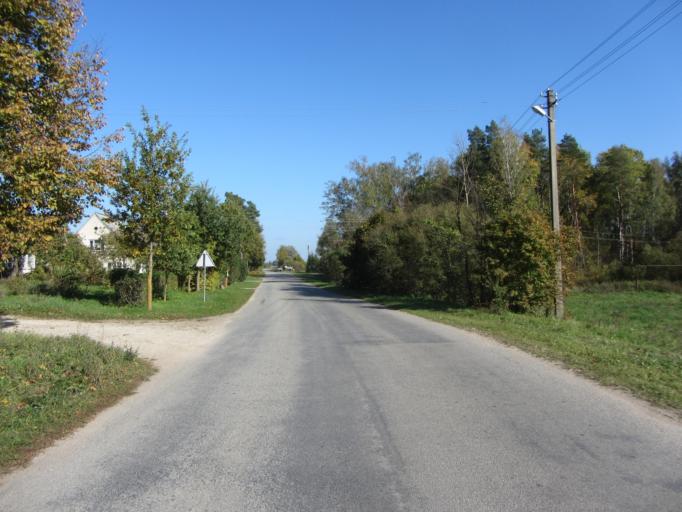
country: LV
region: Nereta
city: Nereta
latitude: 56.0618
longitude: 25.2903
